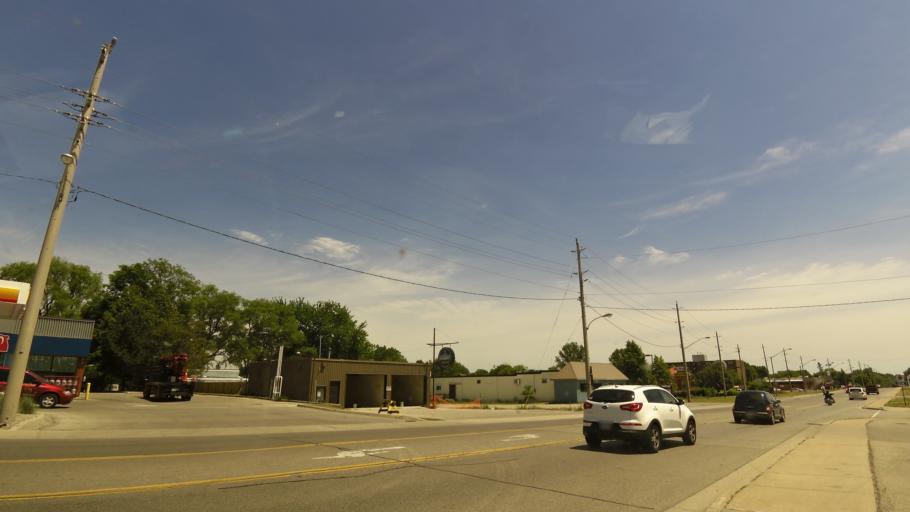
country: CA
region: Ontario
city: Ingersoll
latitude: 42.8775
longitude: -80.7457
